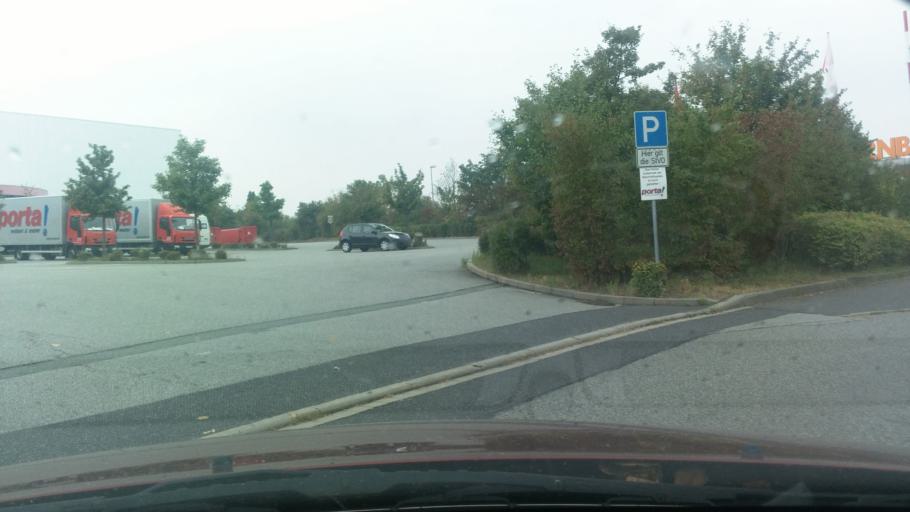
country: DE
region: Saxony
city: Goerlitz
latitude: 51.1897
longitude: 14.9584
